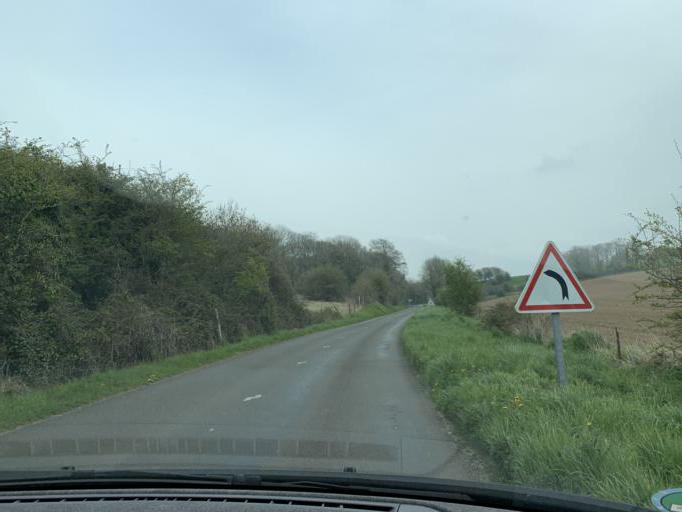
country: FR
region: Haute-Normandie
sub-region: Departement de la Seine-Maritime
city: Saint-Valery-en-Caux
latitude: 49.8528
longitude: 0.7322
